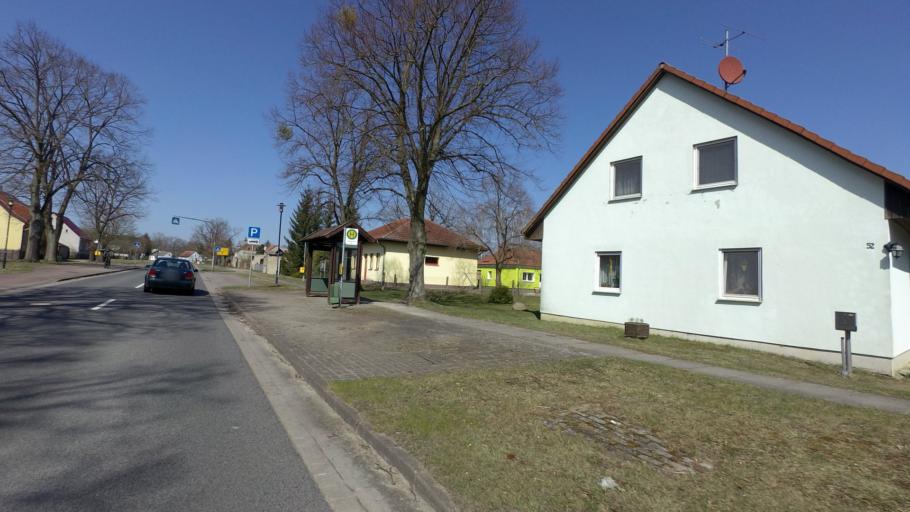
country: DE
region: Brandenburg
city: Lindow
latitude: 52.9344
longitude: 12.9696
